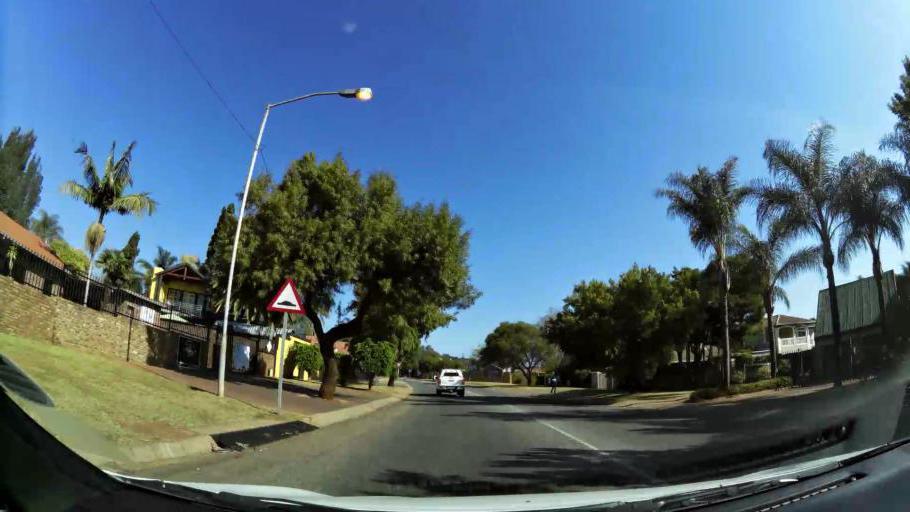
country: ZA
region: Gauteng
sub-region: City of Tshwane Metropolitan Municipality
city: Pretoria
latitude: -25.7917
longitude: 28.2723
